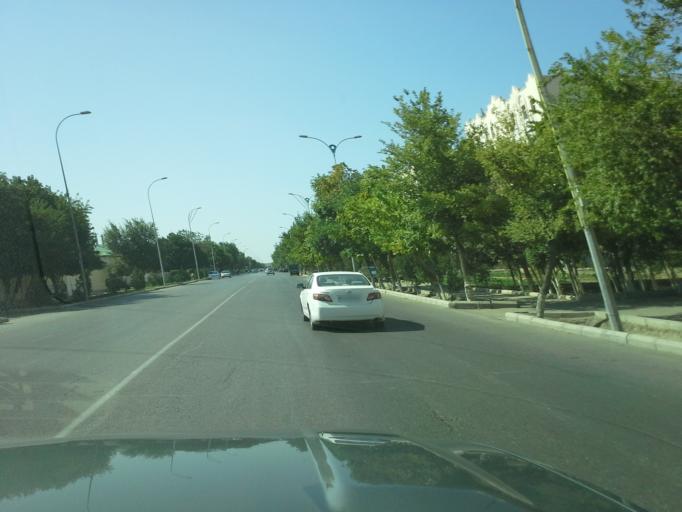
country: TM
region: Dasoguz
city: Dasoguz
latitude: 41.8371
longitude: 59.9561
